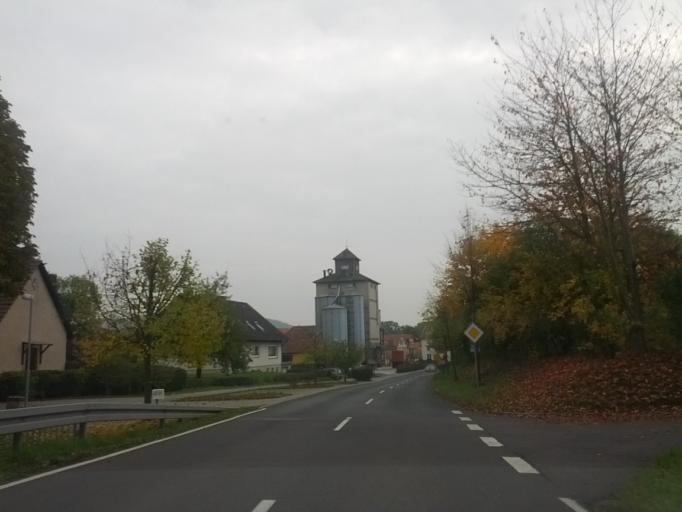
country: DE
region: Hesse
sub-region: Regierungsbezirk Kassel
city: Herleshausen
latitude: 51.0087
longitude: 10.1611
